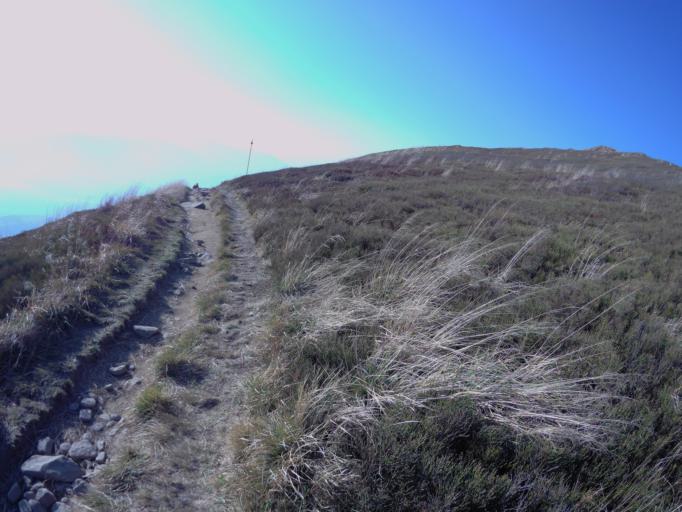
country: PL
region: Subcarpathian Voivodeship
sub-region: Powiat bieszczadzki
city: Lutowiska
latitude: 49.1353
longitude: 22.6075
